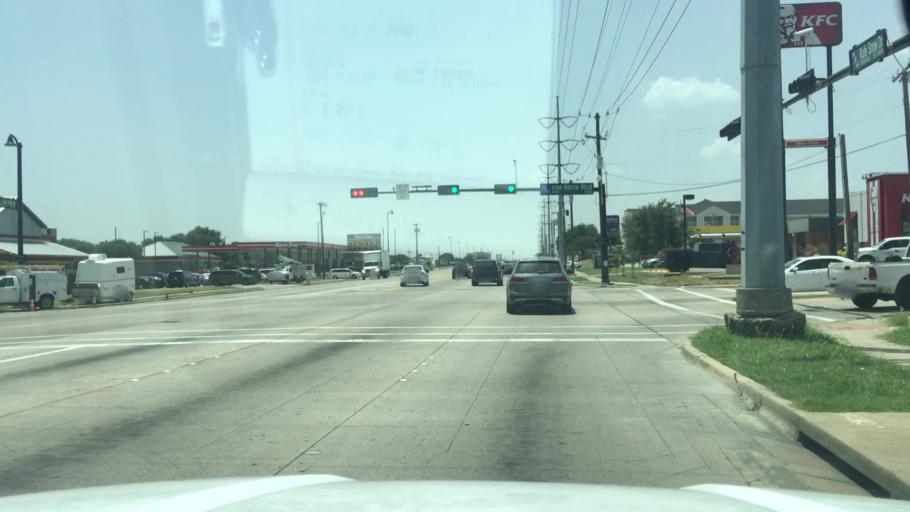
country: US
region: Texas
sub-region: Tarrant County
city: Watauga
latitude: 32.8517
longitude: -97.2387
